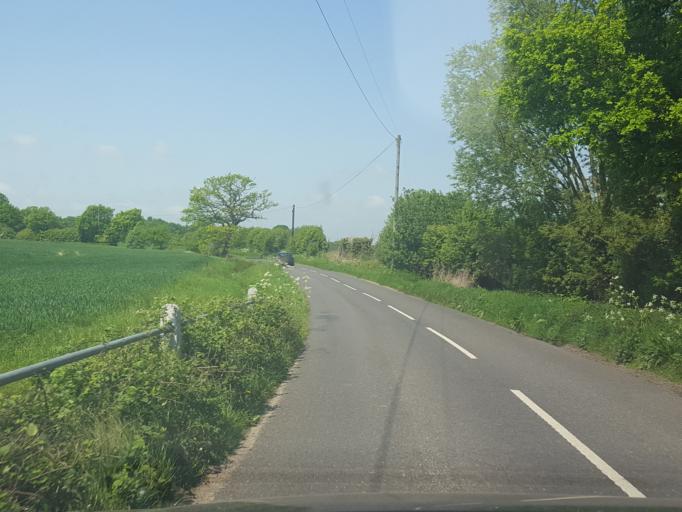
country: GB
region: England
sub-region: Essex
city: Great Bentley
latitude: 51.8553
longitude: 1.0789
